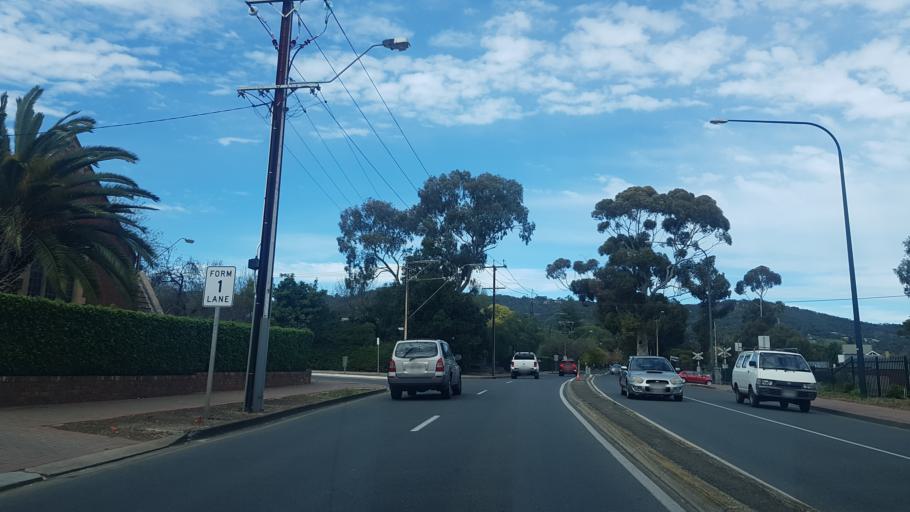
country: AU
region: South Australia
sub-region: Mitcham
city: Hawthorn
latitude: -34.9783
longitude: 138.6099
